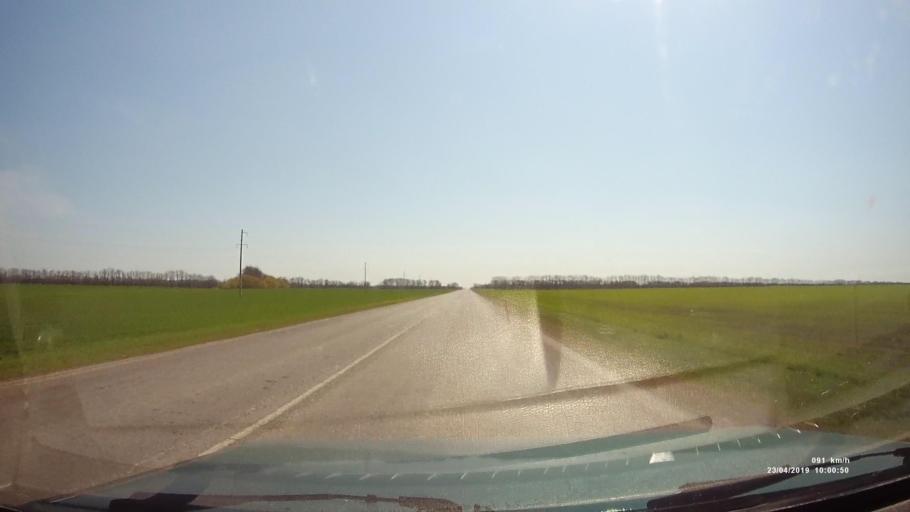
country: RU
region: Rostov
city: Sovetskoye
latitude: 46.7685
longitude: 42.1390
